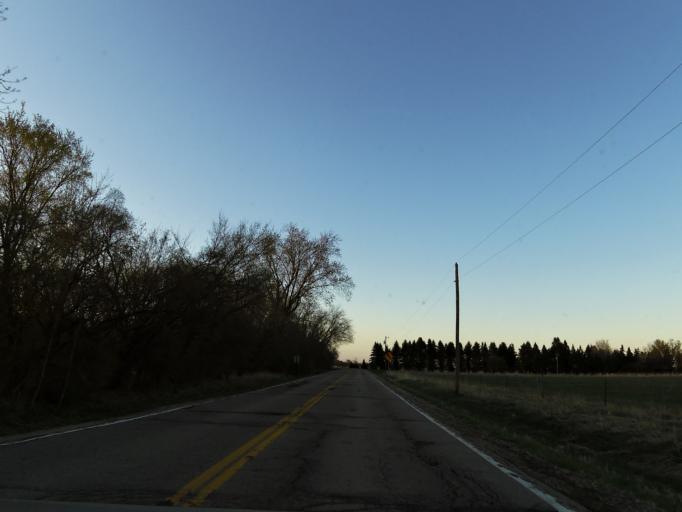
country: US
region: Minnesota
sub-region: Washington County
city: Lakeland
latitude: 44.9457
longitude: -92.7970
